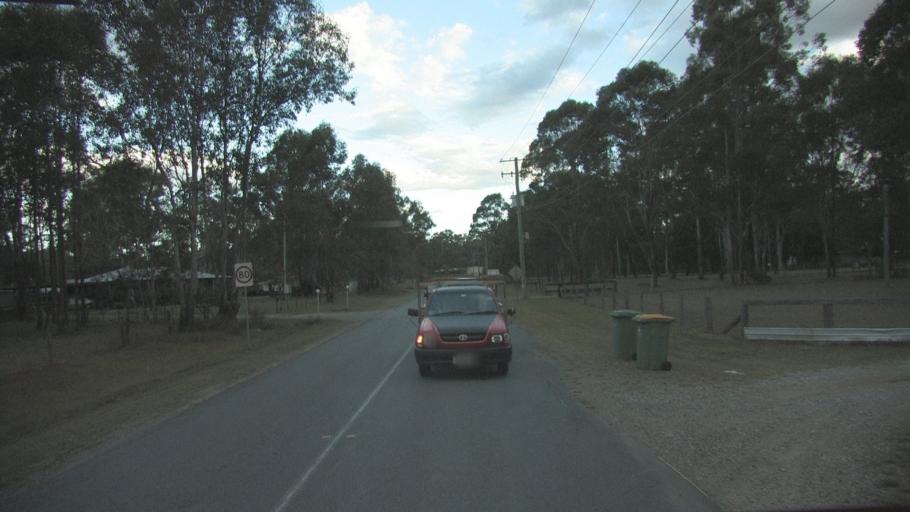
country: AU
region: Queensland
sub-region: Logan
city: Chambers Flat
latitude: -27.7839
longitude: 153.1351
